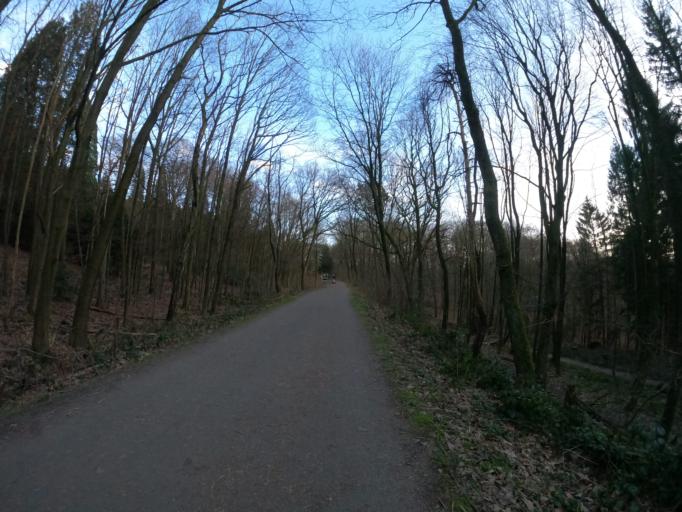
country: DE
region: North Rhine-Westphalia
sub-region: Regierungsbezirk Dusseldorf
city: Wuppertal
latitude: 51.2288
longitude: 7.1233
